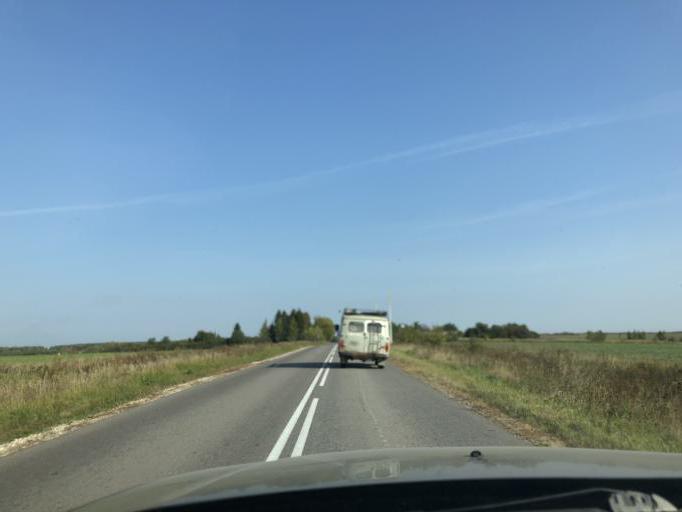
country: RU
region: Tula
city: Novogurovskiy
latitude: 54.4051
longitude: 37.3107
